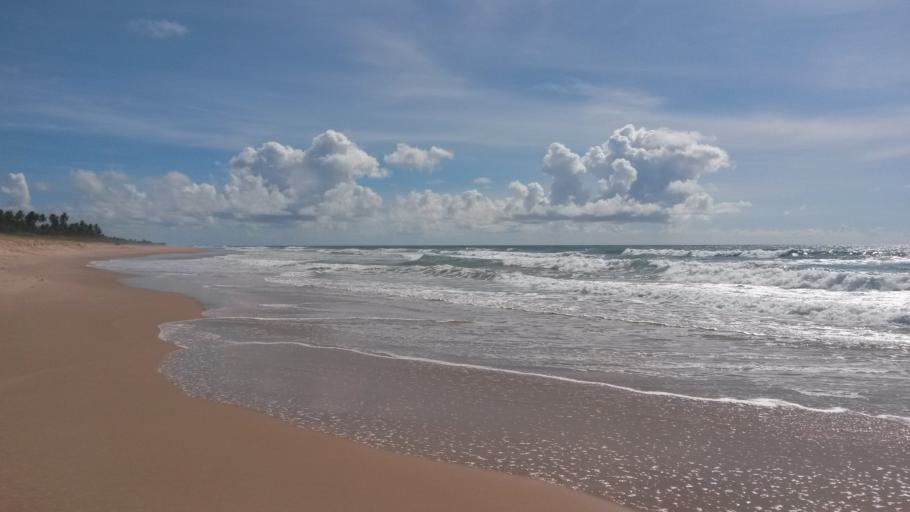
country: BR
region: Bahia
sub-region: Mata De Sao Joao
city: Mata de Sao Joao
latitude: -12.4843
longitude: -37.9502
